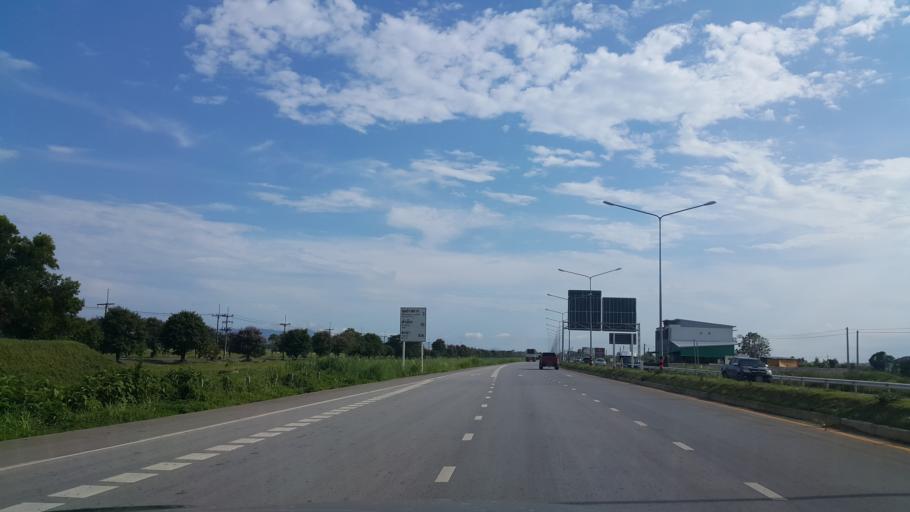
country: TH
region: Chiang Rai
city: Chiang Rai
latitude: 19.9519
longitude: 99.8753
